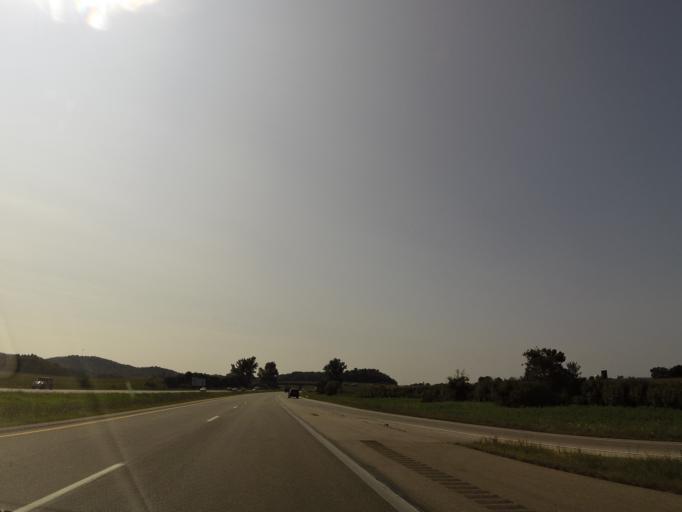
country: US
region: Wisconsin
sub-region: La Crosse County
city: Bangor
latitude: 43.8864
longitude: -91.0047
